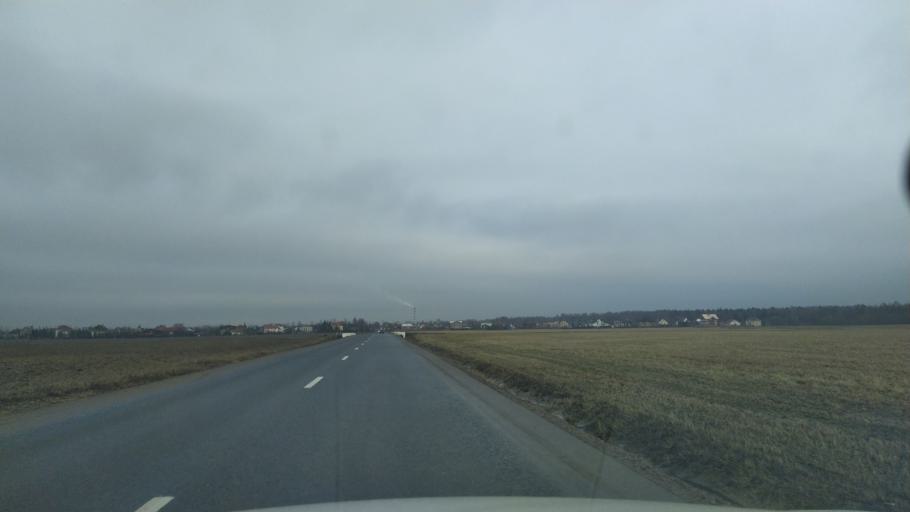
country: RU
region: St.-Petersburg
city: Aleksandrovskaya
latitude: 59.7173
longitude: 30.3389
